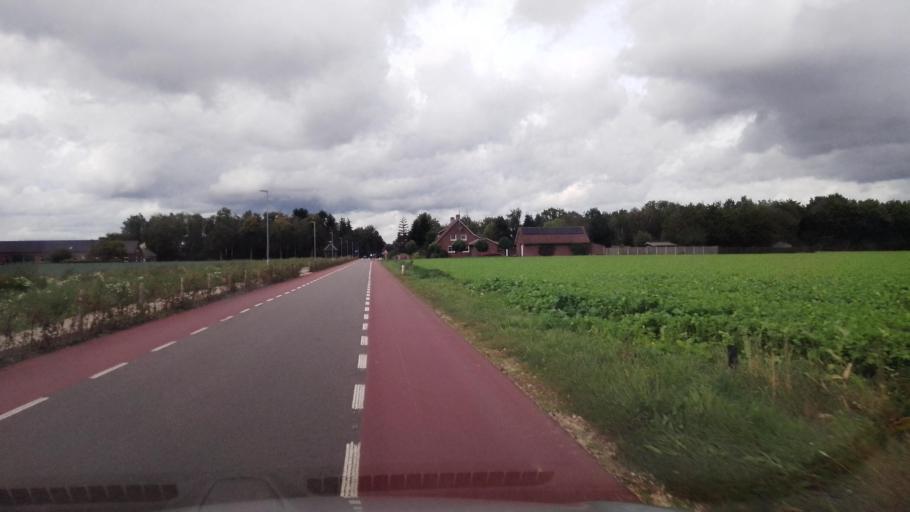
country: NL
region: Limburg
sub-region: Gemeente Peel en Maas
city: Maasbree
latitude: 51.3676
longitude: 6.0523
